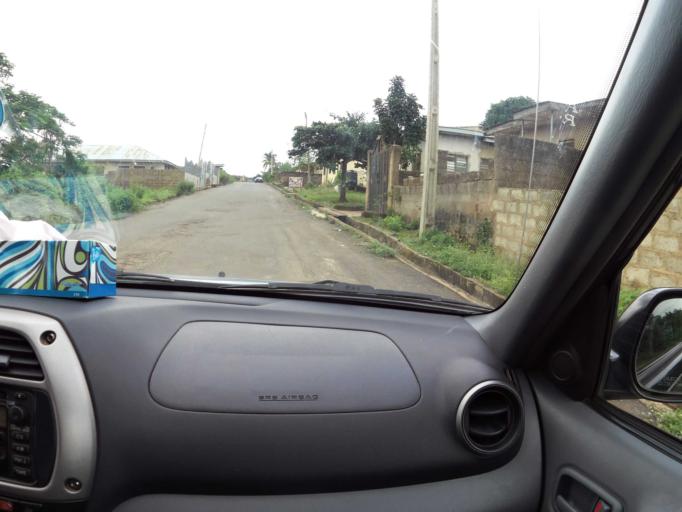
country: NG
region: Oyo
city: Moniya
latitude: 7.5259
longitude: 3.9248
